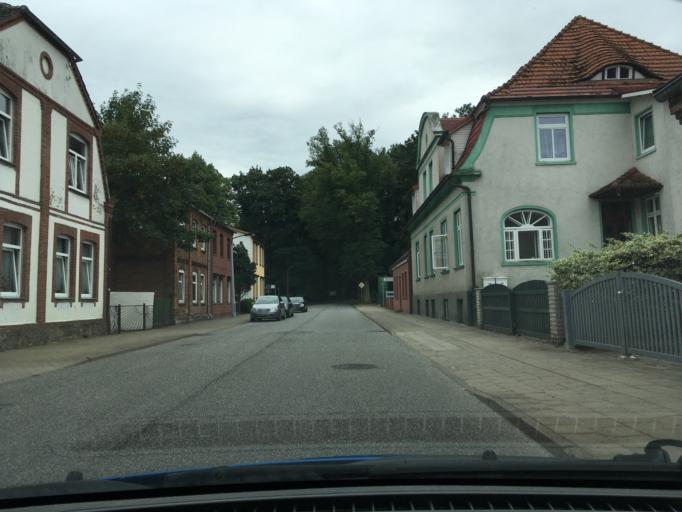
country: DE
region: Mecklenburg-Vorpommern
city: Wittenburg
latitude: 53.5062
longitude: 11.0780
